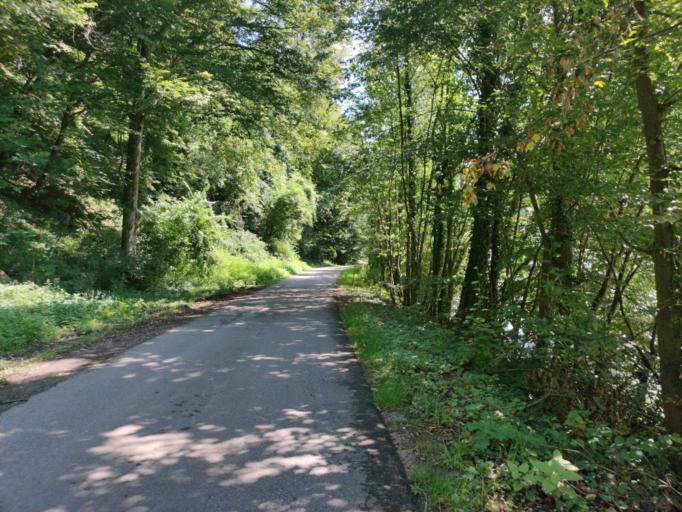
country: AT
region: Upper Austria
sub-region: Politischer Bezirk Rohrbach
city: Pfarrkirchen im Muehlkreis
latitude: 48.4334
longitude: 13.8529
